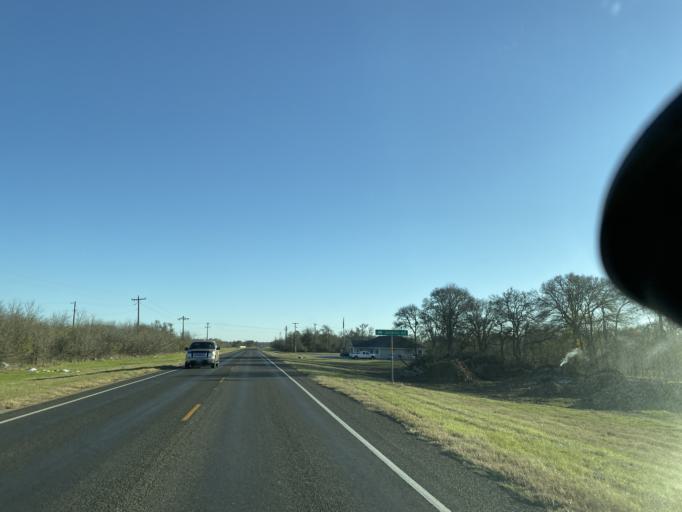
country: US
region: Texas
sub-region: Bastrop County
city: Wyldwood
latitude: 30.0995
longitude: -97.5059
